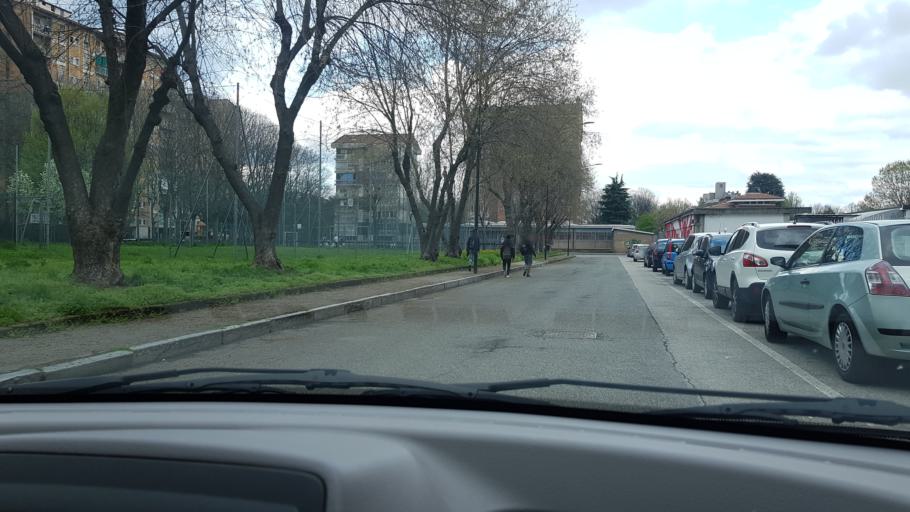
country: IT
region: Piedmont
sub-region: Provincia di Torino
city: Nichelino
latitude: 45.0161
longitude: 7.6357
